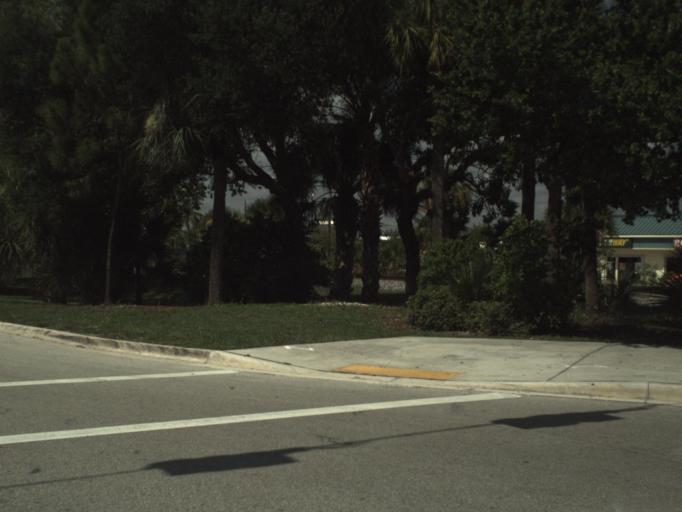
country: US
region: Florida
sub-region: Palm Beach County
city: Jupiter
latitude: 26.9413
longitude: -80.0934
